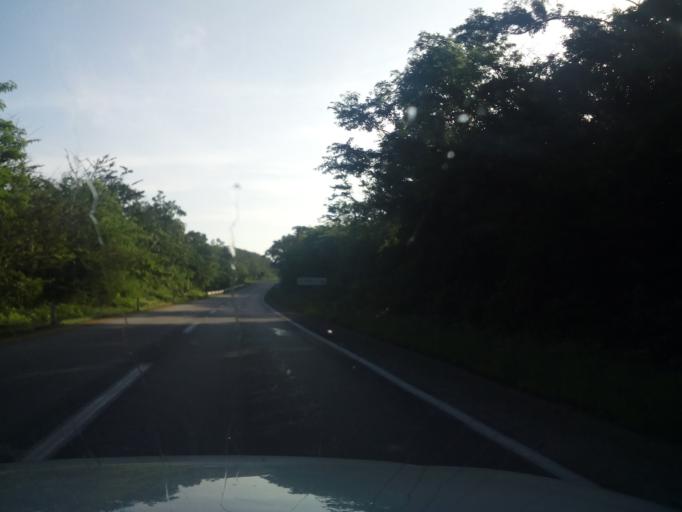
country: MX
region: Yucatan
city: Tinum
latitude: 20.7151
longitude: -88.4181
